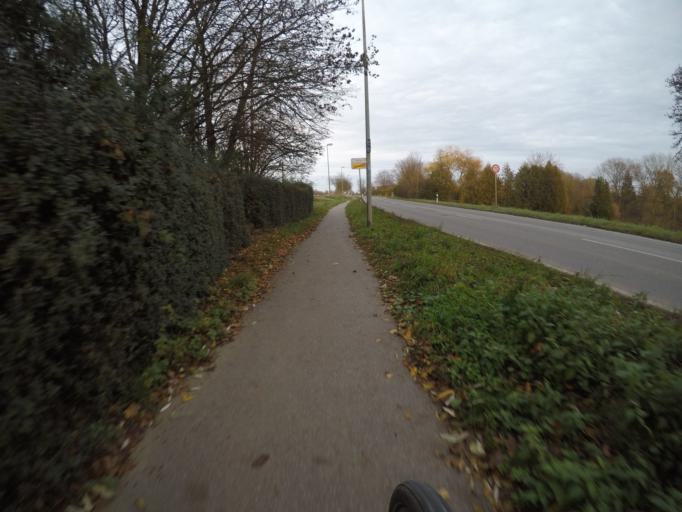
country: DE
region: Baden-Wuerttemberg
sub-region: Regierungsbezirk Stuttgart
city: Ostfildern
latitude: 48.7107
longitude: 9.2720
